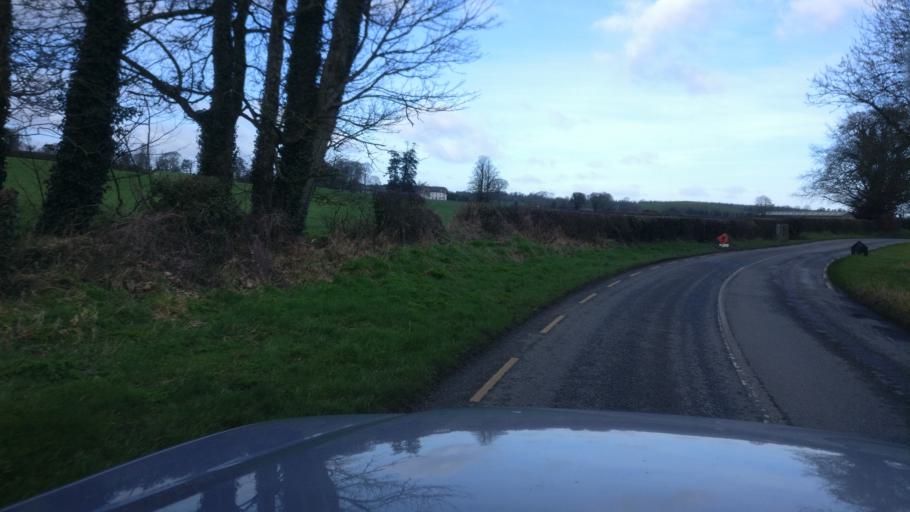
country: IE
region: Leinster
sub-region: Kilkenny
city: Castlecomer
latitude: 52.8234
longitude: -7.2108
